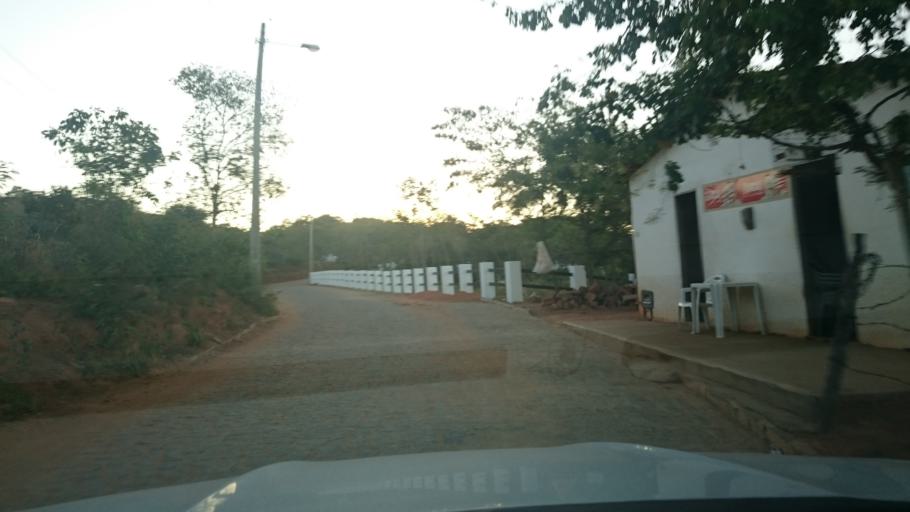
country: BR
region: Rio Grande do Norte
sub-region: Umarizal
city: Umarizal
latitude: -6.0221
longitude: -37.9967
